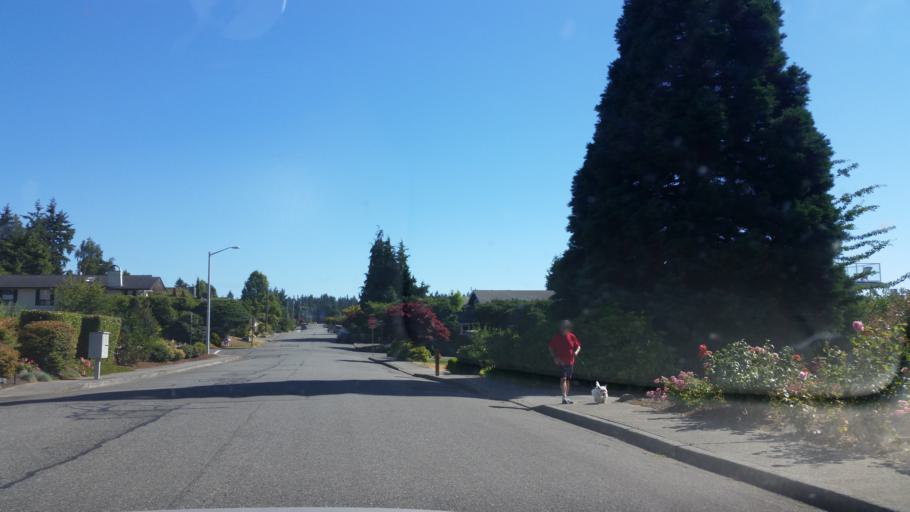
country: US
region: Washington
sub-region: Snohomish County
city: Edmonds
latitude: 47.8039
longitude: -122.3696
